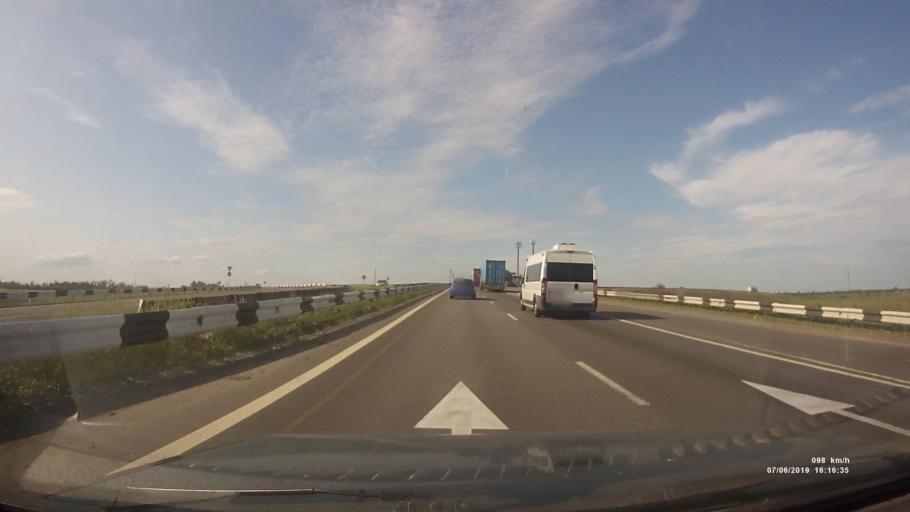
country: RU
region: Rostov
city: Likhoy
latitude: 48.1875
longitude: 40.2644
